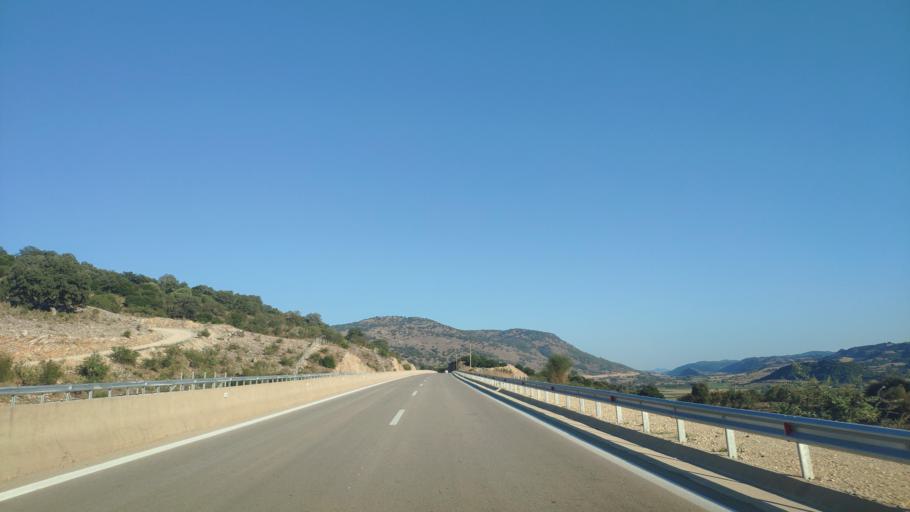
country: GR
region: West Greece
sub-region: Nomos Aitolias kai Akarnanias
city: Katouna
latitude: 38.8461
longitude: 21.1000
